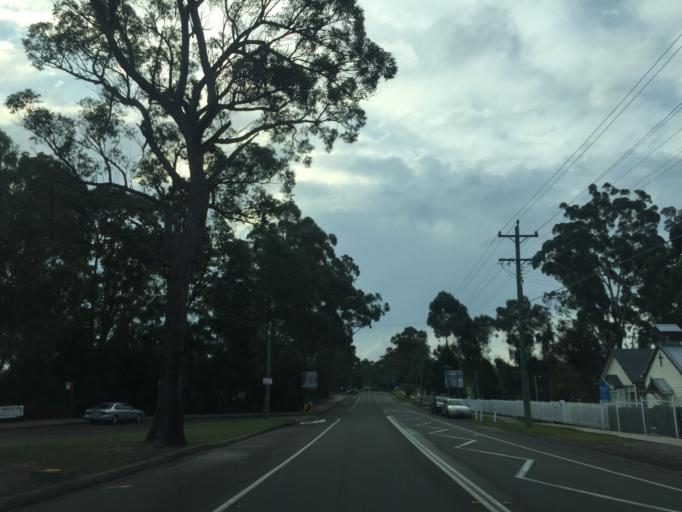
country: AU
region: New South Wales
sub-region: The Hills Shire
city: Glenhaven
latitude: -33.6998
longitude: 151.0032
